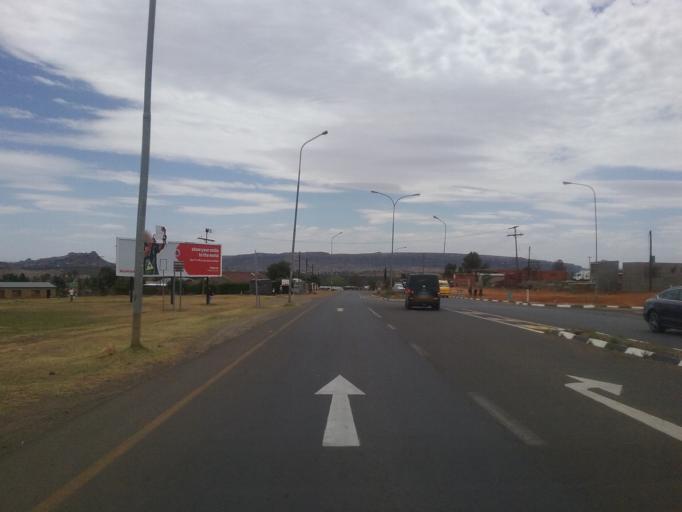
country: LS
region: Maseru
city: Maseru
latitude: -29.4234
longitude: 27.5619
